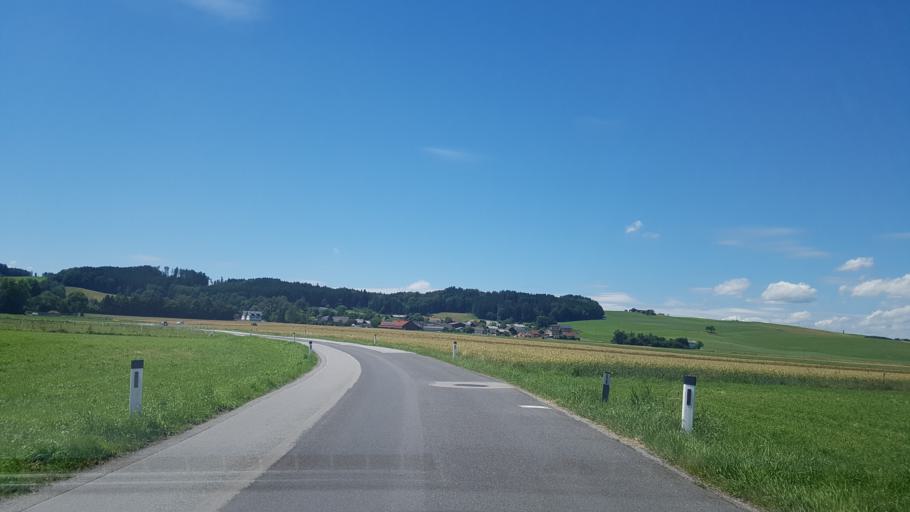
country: AT
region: Salzburg
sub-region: Politischer Bezirk Salzburg-Umgebung
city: Schleedorf
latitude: 48.0066
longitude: 13.1699
